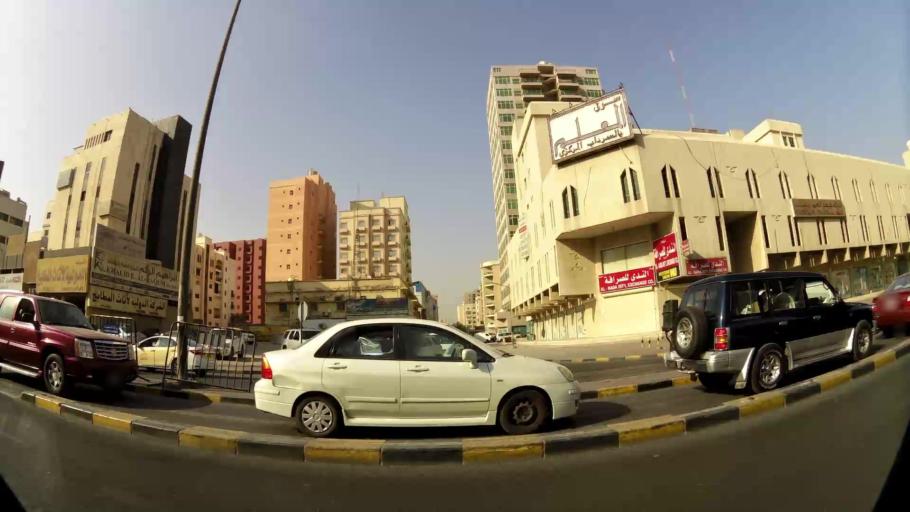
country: KW
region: Muhafazat Hawalli
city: Hawalli
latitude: 29.3337
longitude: 48.0265
